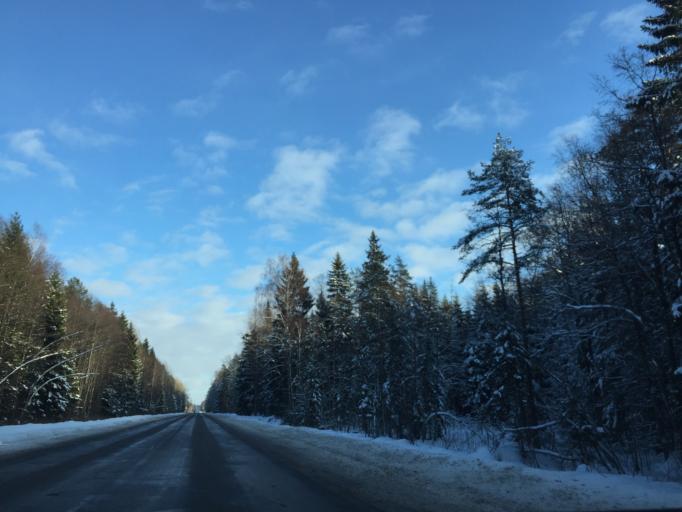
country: LV
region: Ikskile
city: Ikskile
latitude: 56.9491
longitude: 24.4967
